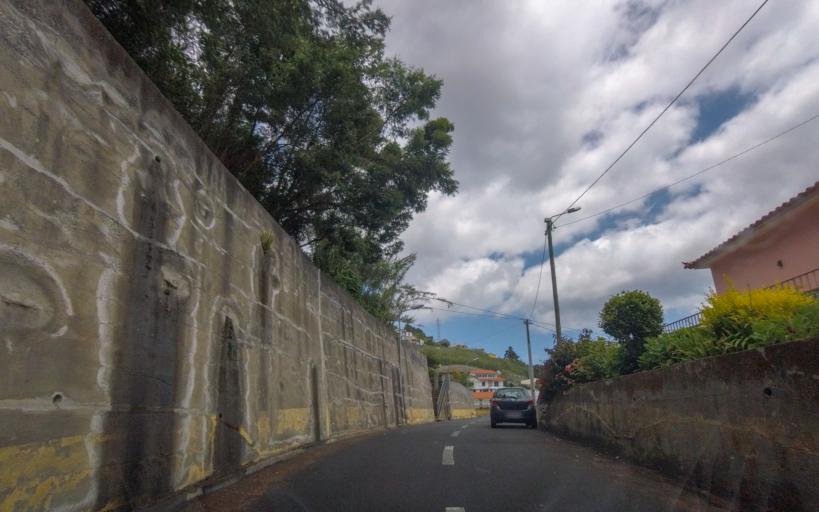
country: PT
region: Madeira
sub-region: Funchal
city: Nossa Senhora do Monte
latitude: 32.6632
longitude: -16.8833
